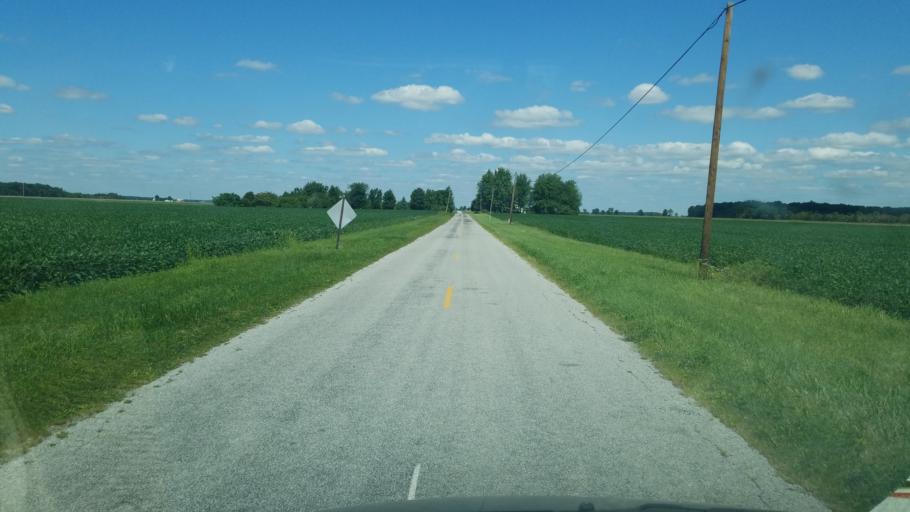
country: US
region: Ohio
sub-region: Fulton County
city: Delta
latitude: 41.7099
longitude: -84.0178
